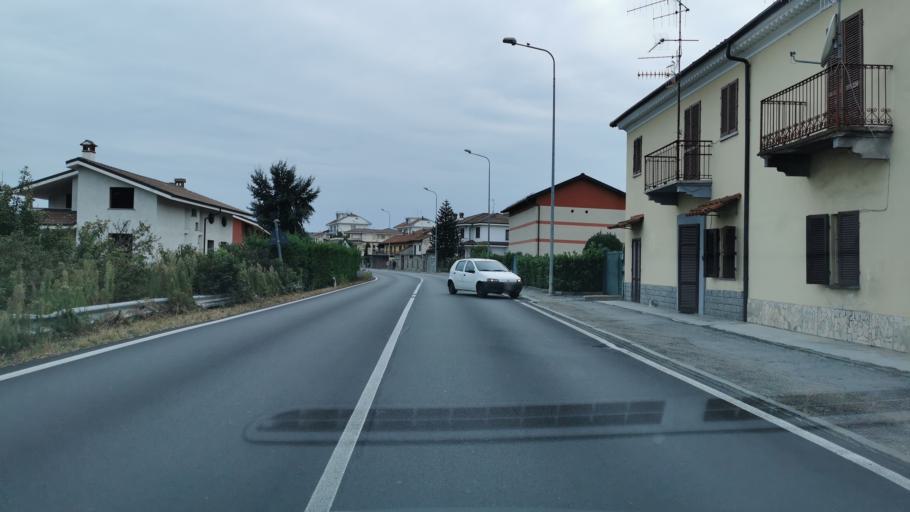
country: IT
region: Piedmont
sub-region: Provincia di Cuneo
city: Bra
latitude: 44.6875
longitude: 7.8533
